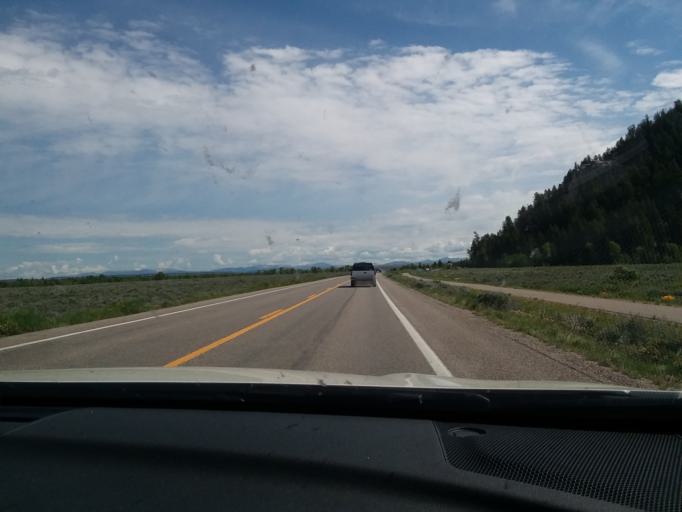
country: US
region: Wyoming
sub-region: Teton County
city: Jackson
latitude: 43.6585
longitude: -110.7011
